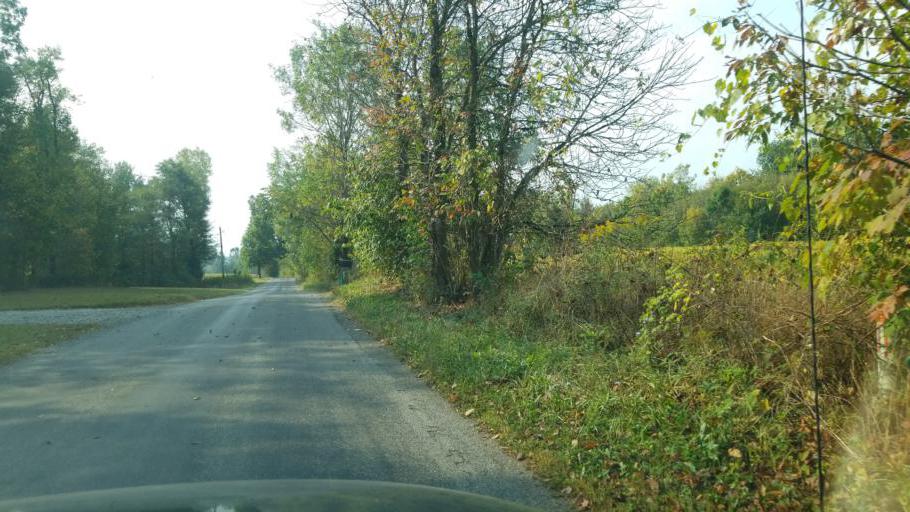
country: US
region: Ohio
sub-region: Licking County
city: Utica
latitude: 40.2518
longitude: -82.5759
